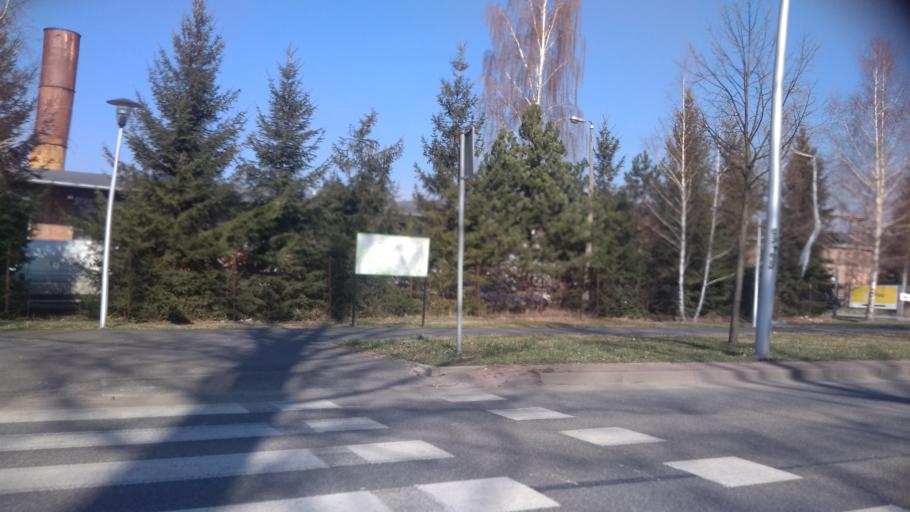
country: PL
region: Lower Silesian Voivodeship
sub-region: Jelenia Gora
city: Jelenia Gora
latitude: 50.8851
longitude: 15.7057
